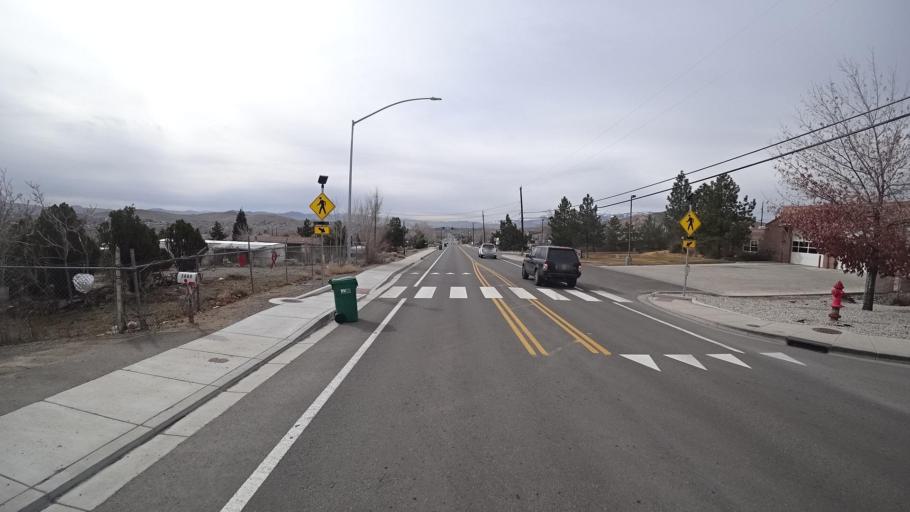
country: US
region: Nevada
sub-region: Washoe County
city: Sun Valley
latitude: 39.6054
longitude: -119.7807
